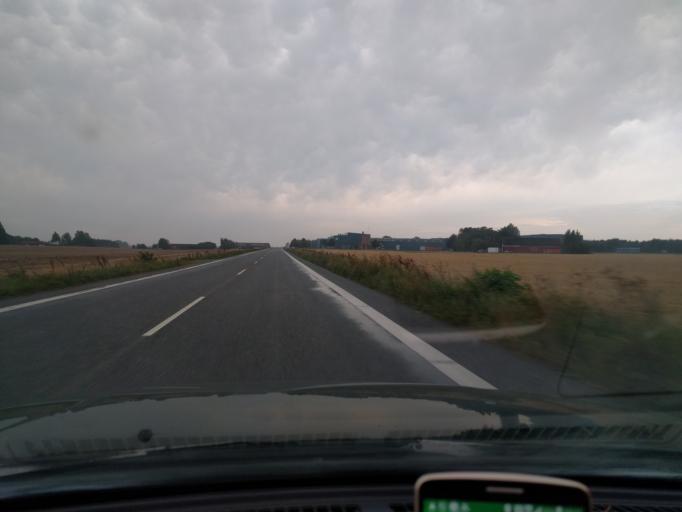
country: DK
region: Zealand
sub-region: Guldborgsund Kommune
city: Norre Alslev
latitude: 54.9140
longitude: 11.8763
